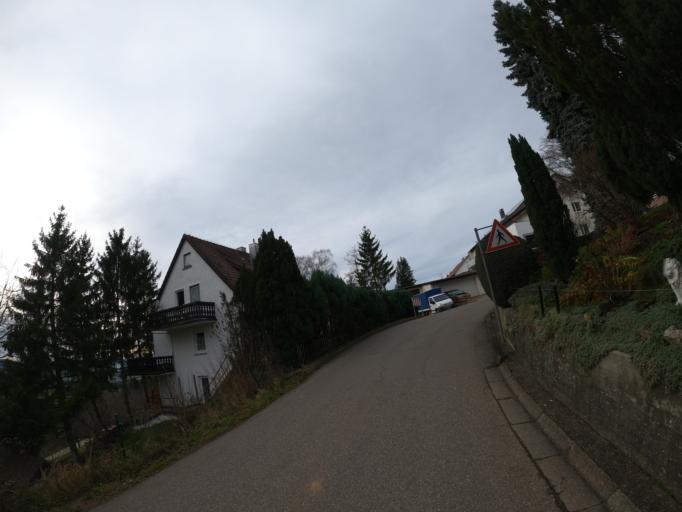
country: DE
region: Baden-Wuerttemberg
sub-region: Regierungsbezirk Stuttgart
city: Ottenbach
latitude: 48.7539
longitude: 9.7815
